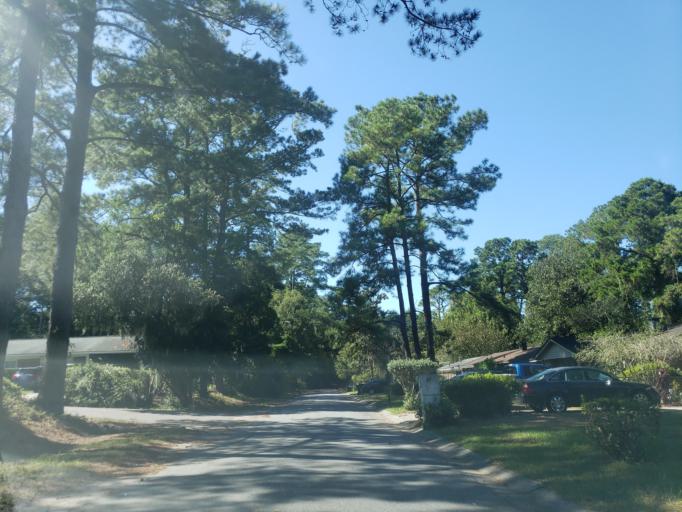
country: US
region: Georgia
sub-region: Chatham County
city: Thunderbolt
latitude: 32.0376
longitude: -81.0731
